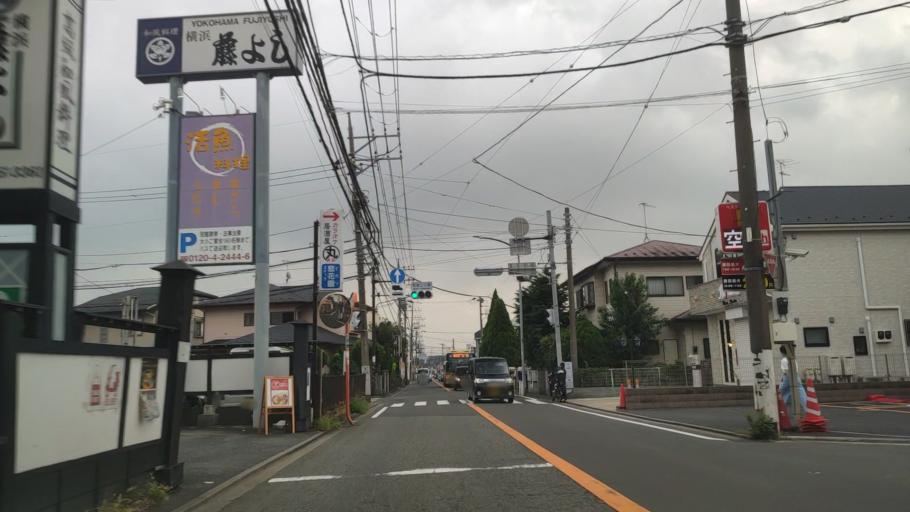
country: JP
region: Kanagawa
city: Minami-rinkan
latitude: 35.4191
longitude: 139.5004
